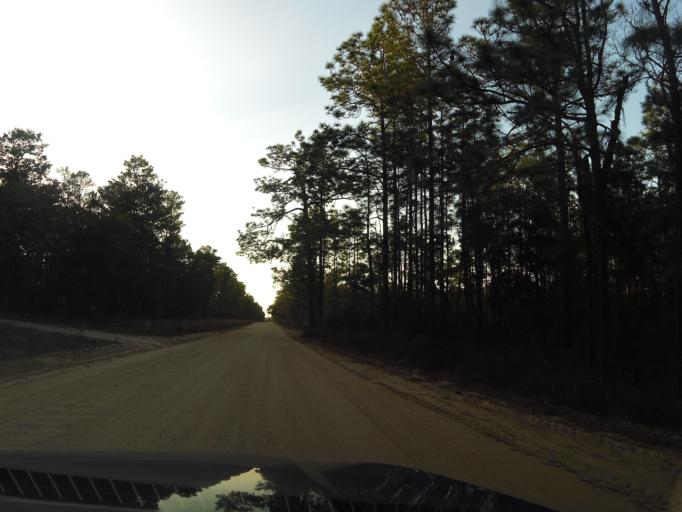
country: US
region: Florida
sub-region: Putnam County
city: Interlachen
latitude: 29.7848
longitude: -81.8666
